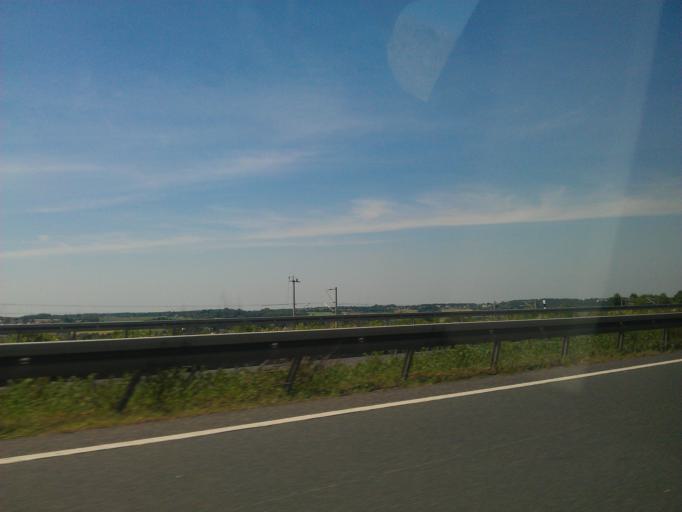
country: DE
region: North Rhine-Westphalia
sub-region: Regierungsbezirk Koln
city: Stossdorf
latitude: 50.7195
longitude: 7.2404
